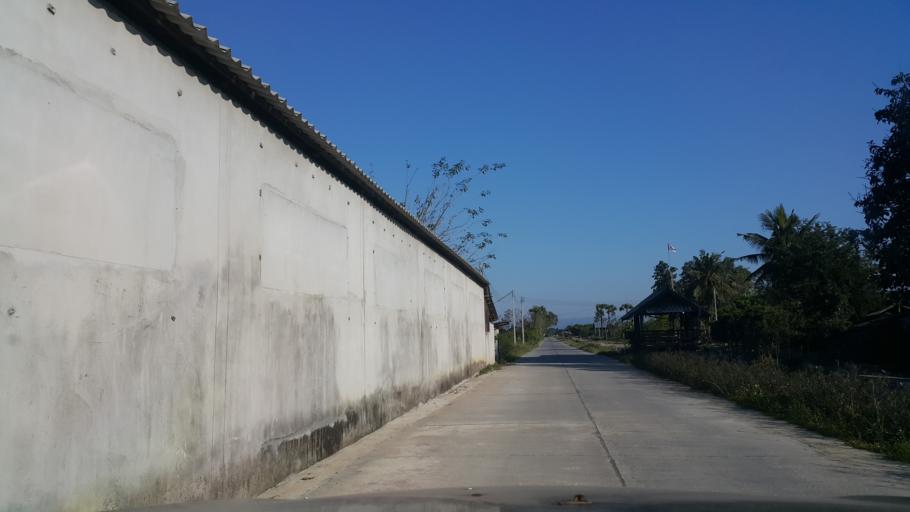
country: TH
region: Chiang Mai
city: Hang Dong
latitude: 18.6781
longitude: 98.9577
